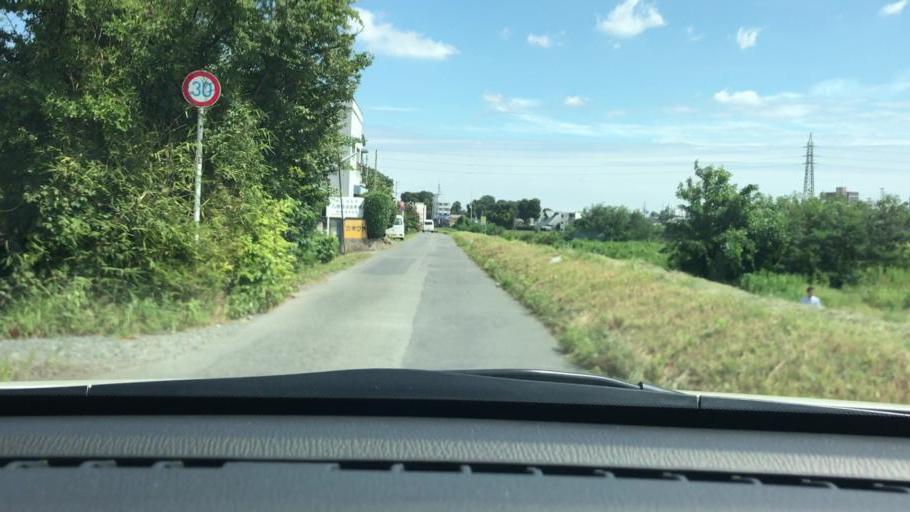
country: JP
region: Tokyo
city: Hachioji
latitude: 35.6668
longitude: 139.3239
